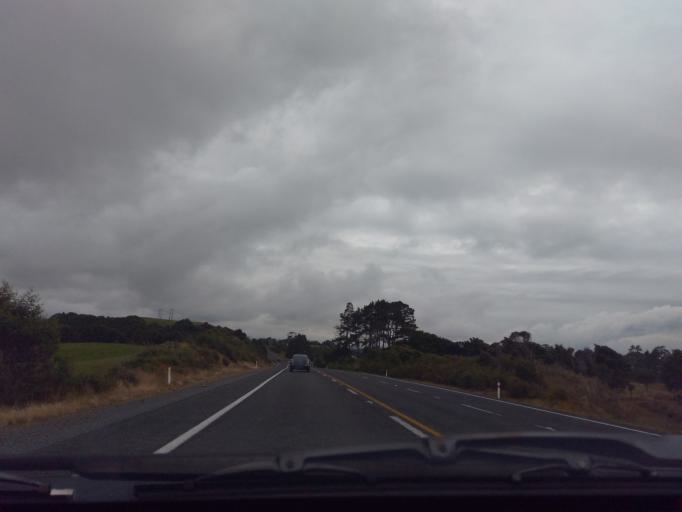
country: NZ
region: Northland
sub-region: Whangarei
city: Ruakaka
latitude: -35.9224
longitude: 174.4533
